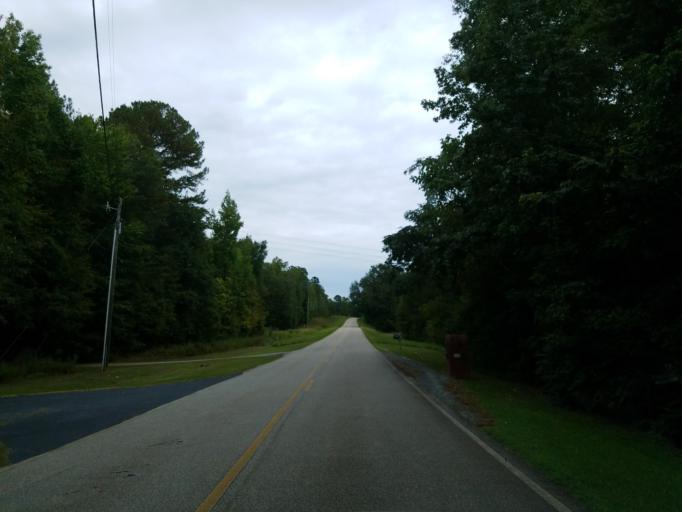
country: US
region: Georgia
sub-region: Bibb County
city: West Point
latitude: 32.9057
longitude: -83.8538
